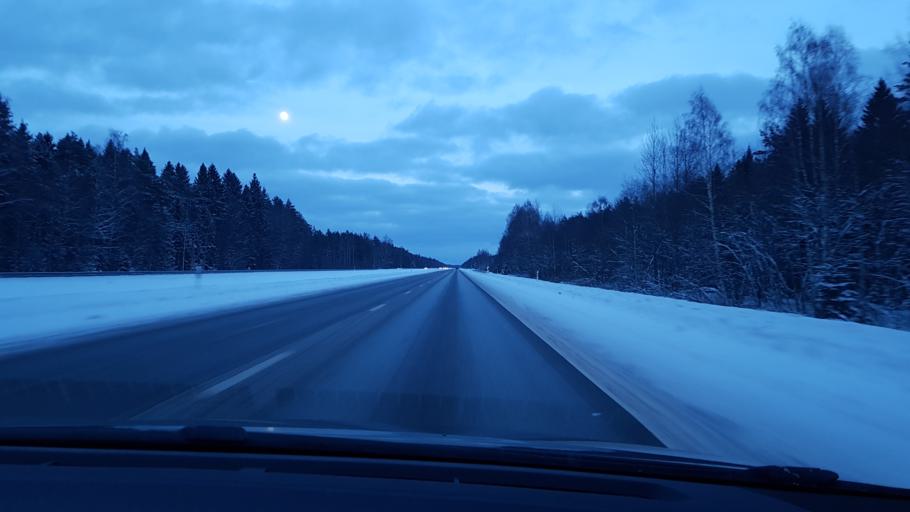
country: EE
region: Harju
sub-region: Kuusalu vald
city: Kuusalu
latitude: 59.4576
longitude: 25.5444
